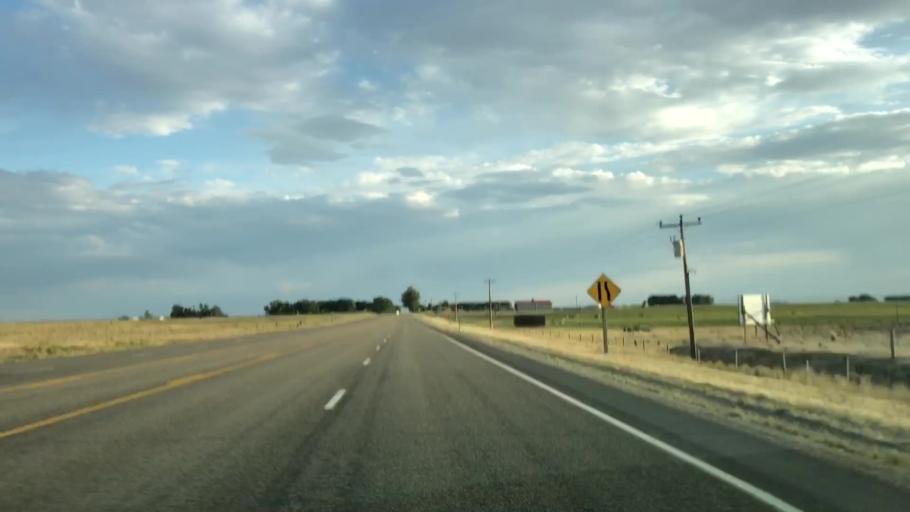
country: US
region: Wyoming
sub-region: Sweetwater County
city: North Rock Springs
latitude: 42.0641
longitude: -109.4382
